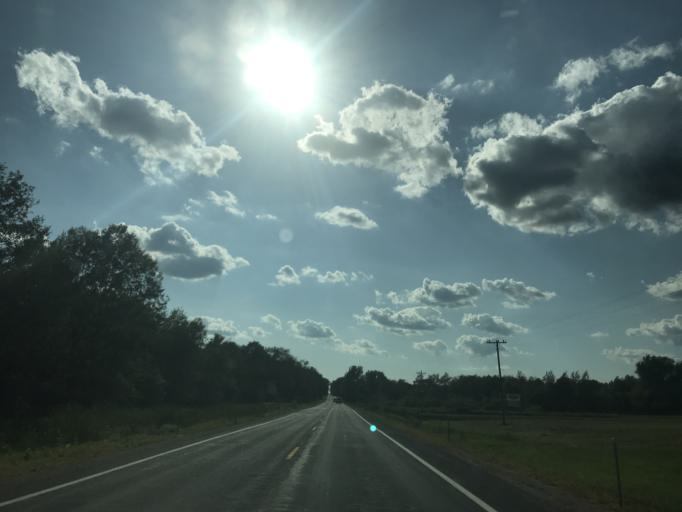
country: US
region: Michigan
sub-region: Newaygo County
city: White Cloud
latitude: 43.5685
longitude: -85.7797
